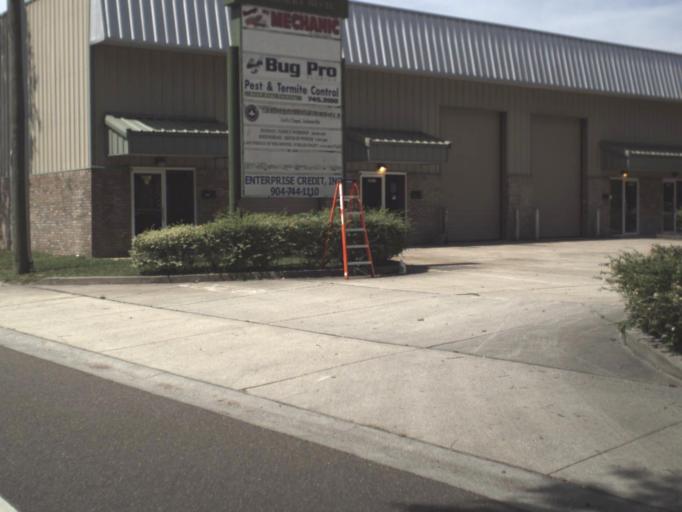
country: US
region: Florida
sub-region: Duval County
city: Jacksonville
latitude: 30.3285
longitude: -81.5970
